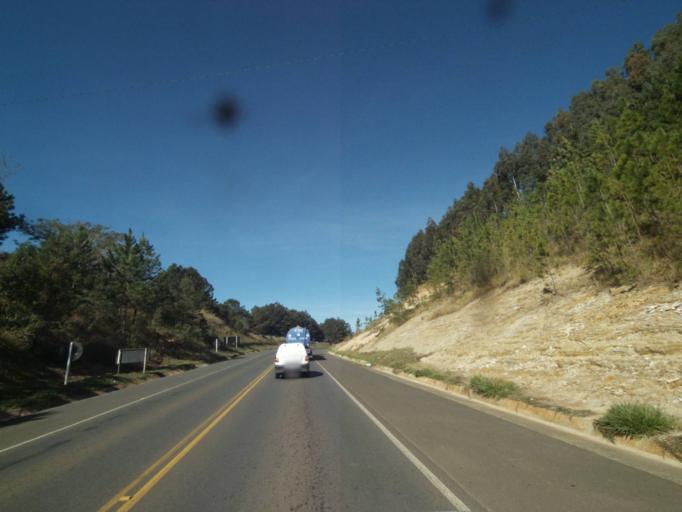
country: BR
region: Parana
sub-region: Tibagi
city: Tibagi
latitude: -24.5017
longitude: -50.4430
